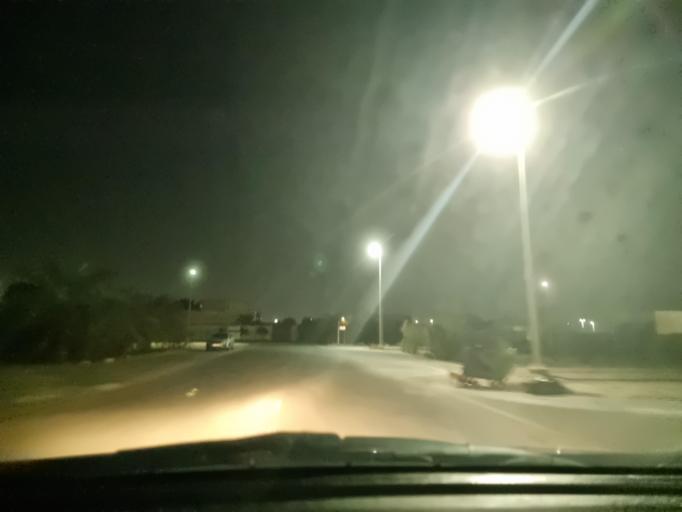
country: AE
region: Abu Dhabi
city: Abu Dhabi
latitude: 24.3827
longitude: 54.6990
